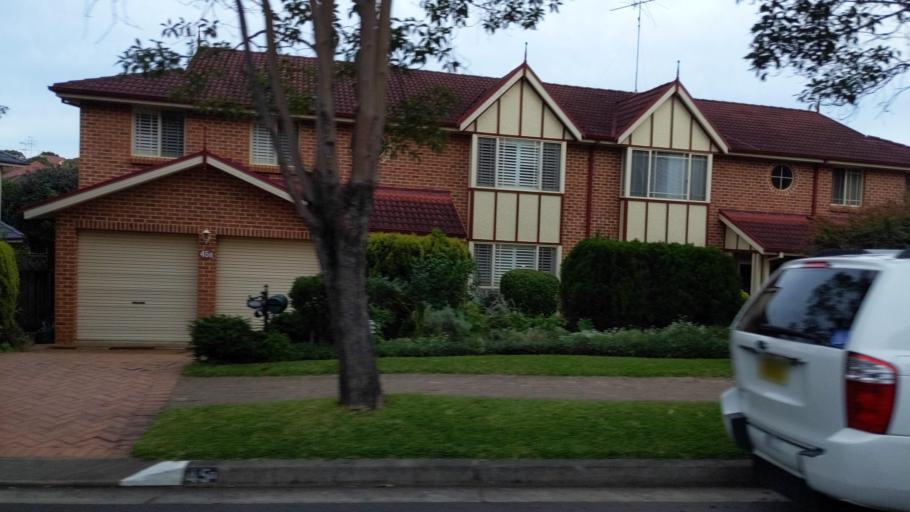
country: AU
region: New South Wales
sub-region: The Hills Shire
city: Baulkham Hills
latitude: -33.7406
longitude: 150.9614
